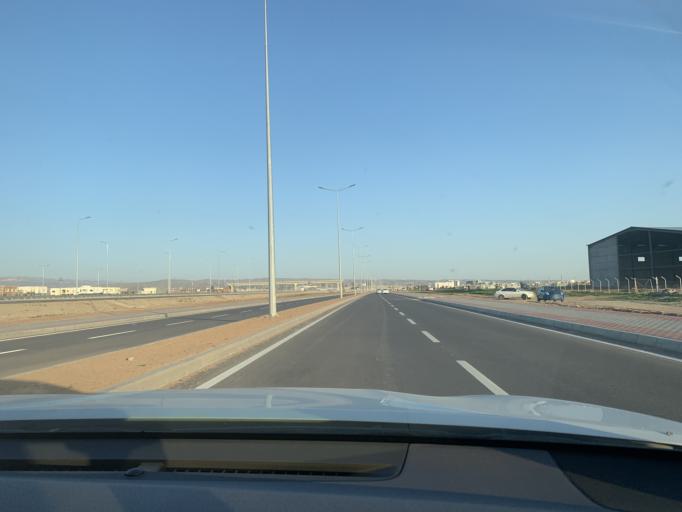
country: IQ
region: Arbil
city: Erbil
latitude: 36.2840
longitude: 44.0523
